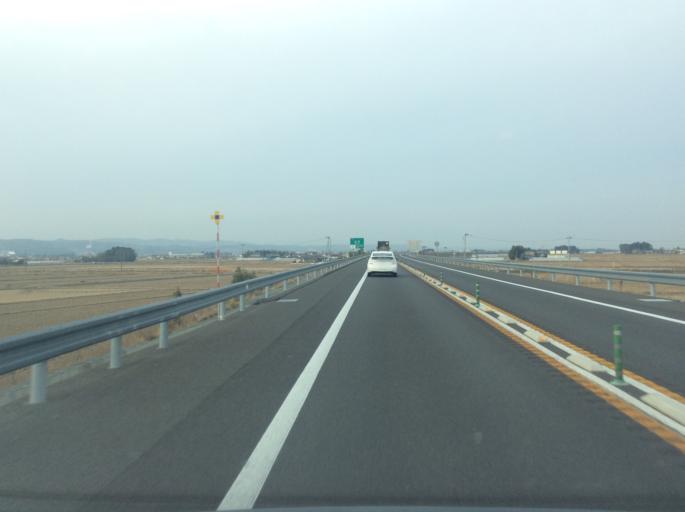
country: JP
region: Miyagi
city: Iwanuma
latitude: 38.0750
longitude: 140.8901
